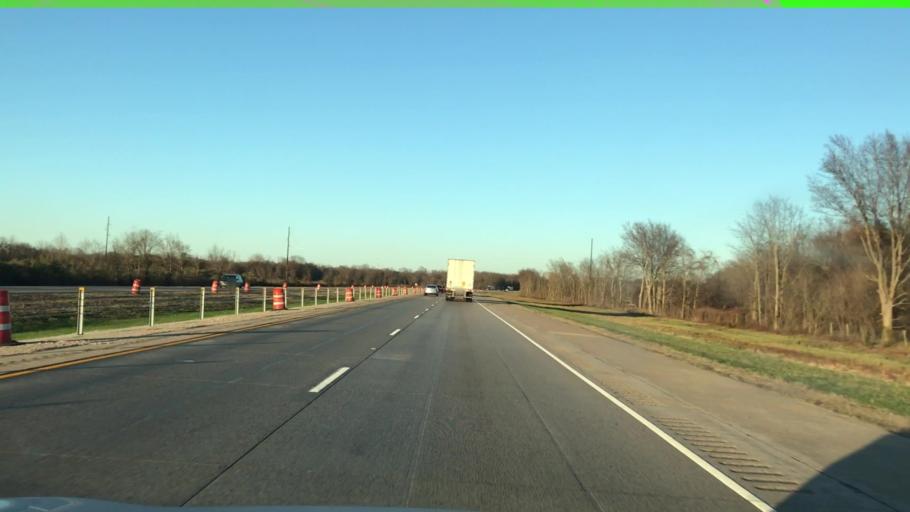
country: US
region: Arkansas
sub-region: Miller County
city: Texarkana
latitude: 33.5799
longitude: -93.8437
